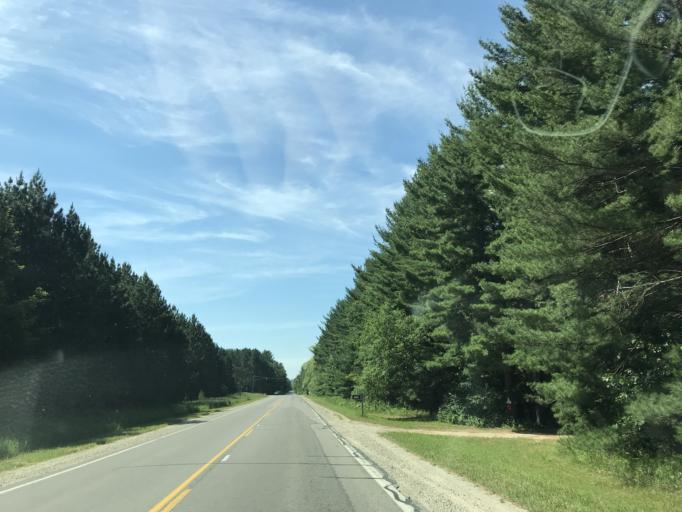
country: US
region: Michigan
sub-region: Grand Traverse County
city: Traverse City
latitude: 44.6565
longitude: -85.7170
